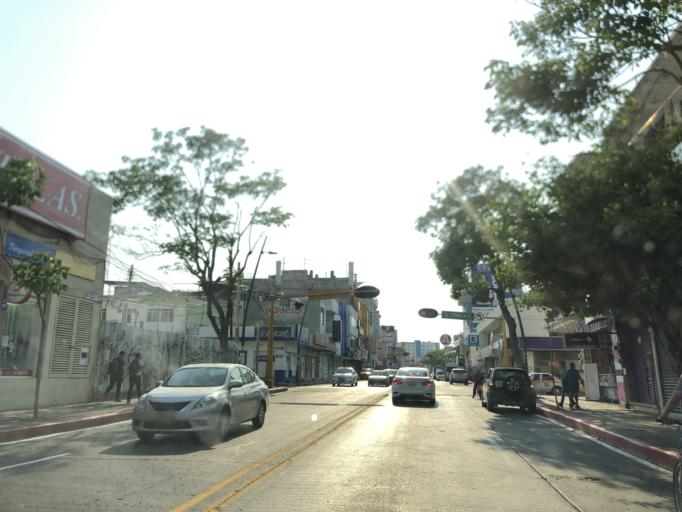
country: MX
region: Chiapas
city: Tuxtla Gutierrez
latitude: 16.7545
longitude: -93.1217
